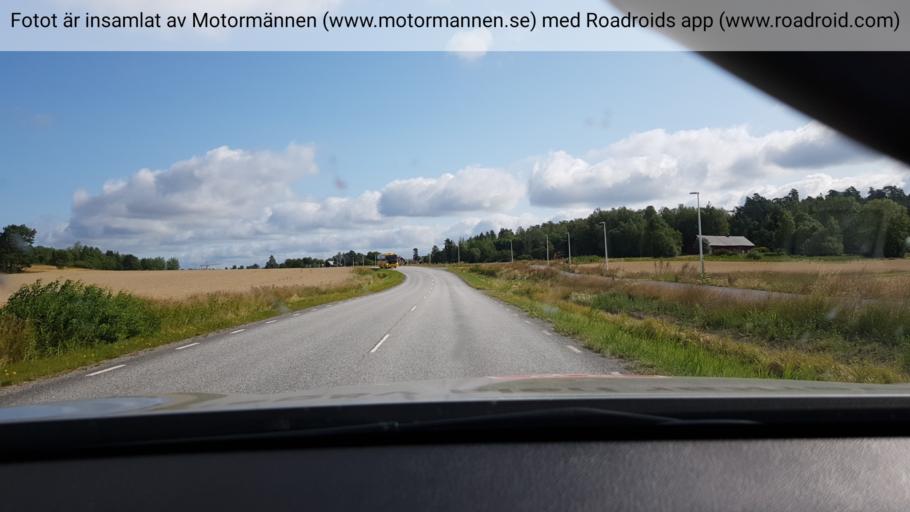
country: SE
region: Uppsala
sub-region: Knivsta Kommun
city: Knivsta
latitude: 59.7161
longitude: 17.7684
